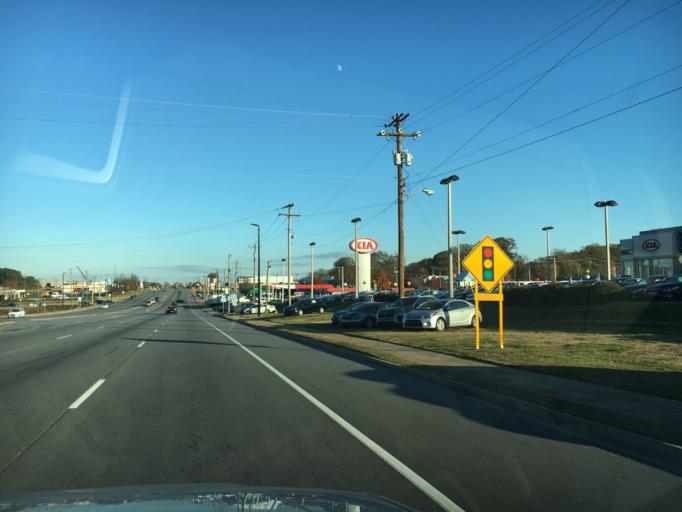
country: US
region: South Carolina
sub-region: Greenville County
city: Greer
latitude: 34.9477
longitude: -82.2172
